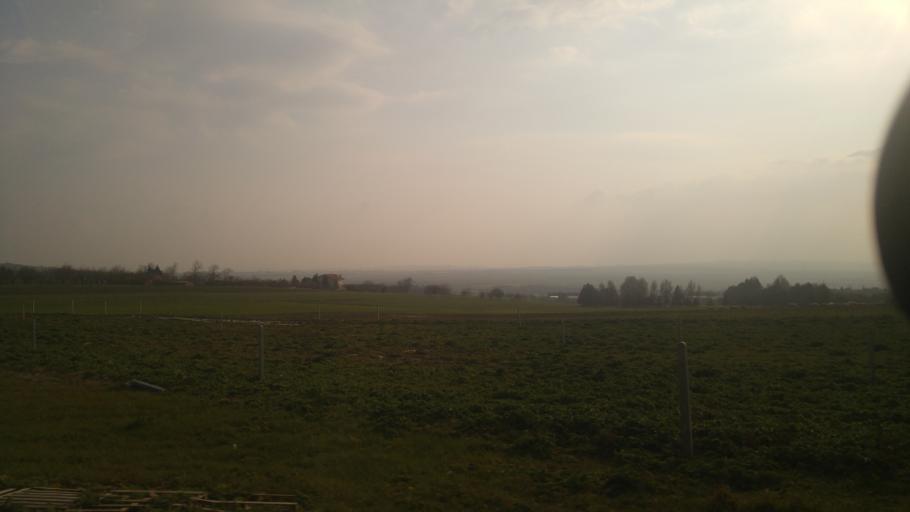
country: TR
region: Istanbul
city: Kavakli
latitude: 41.1301
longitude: 28.3291
